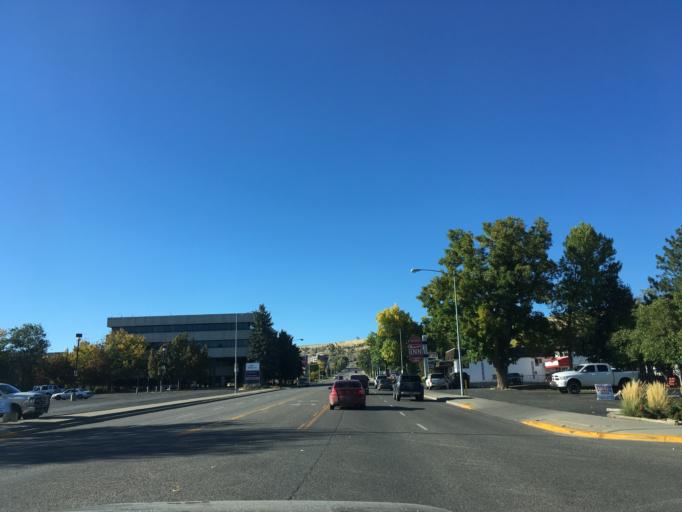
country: US
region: Montana
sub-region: Yellowstone County
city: Billings
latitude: 45.7910
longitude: -108.5127
